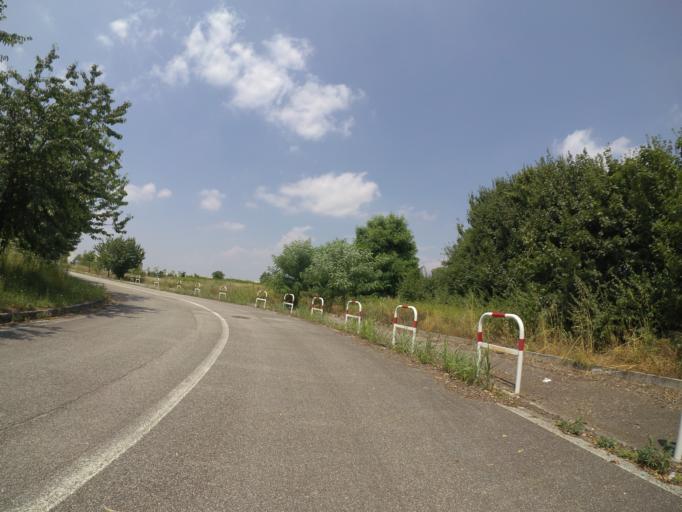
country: IT
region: Friuli Venezia Giulia
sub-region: Provincia di Udine
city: Bertiolo
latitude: 45.9504
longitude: 13.0688
